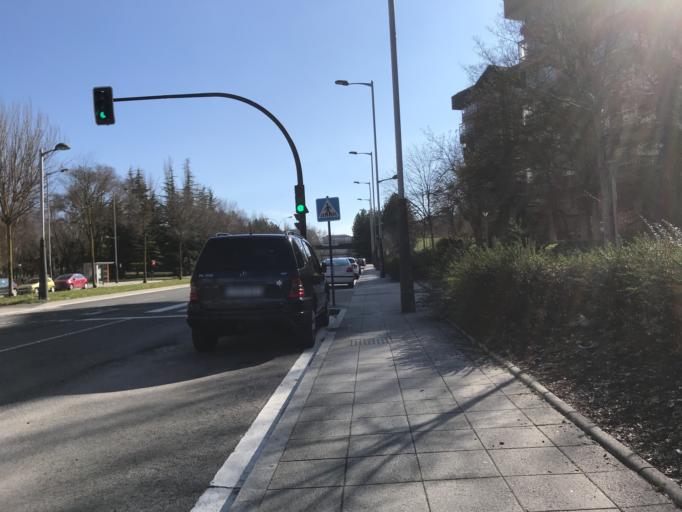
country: ES
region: Basque Country
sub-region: Provincia de Alava
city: Gasteiz / Vitoria
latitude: 42.8534
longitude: -2.6577
